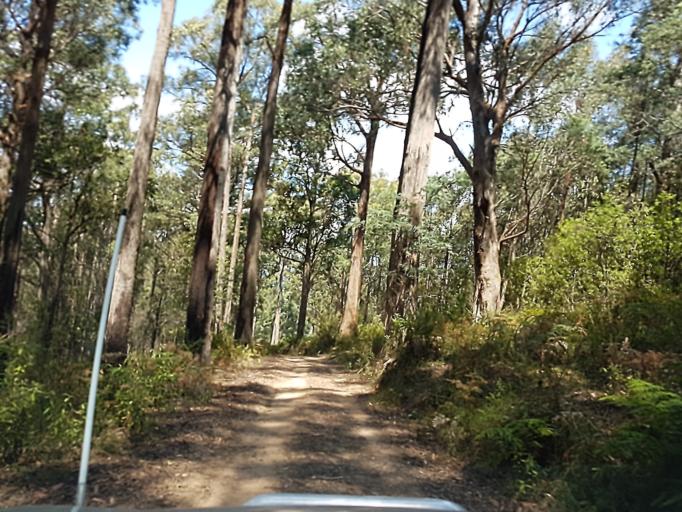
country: AU
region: Victoria
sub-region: East Gippsland
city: Lakes Entrance
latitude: -37.3912
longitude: 148.2923
